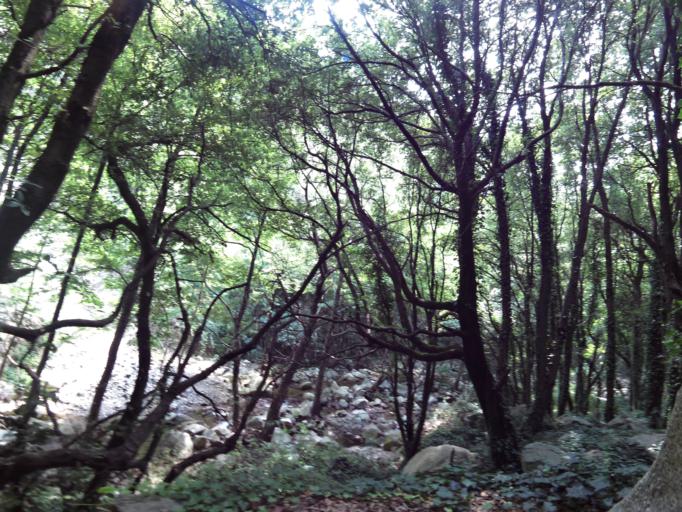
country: IT
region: Calabria
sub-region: Provincia di Reggio Calabria
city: Bivongi
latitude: 38.5017
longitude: 16.3983
